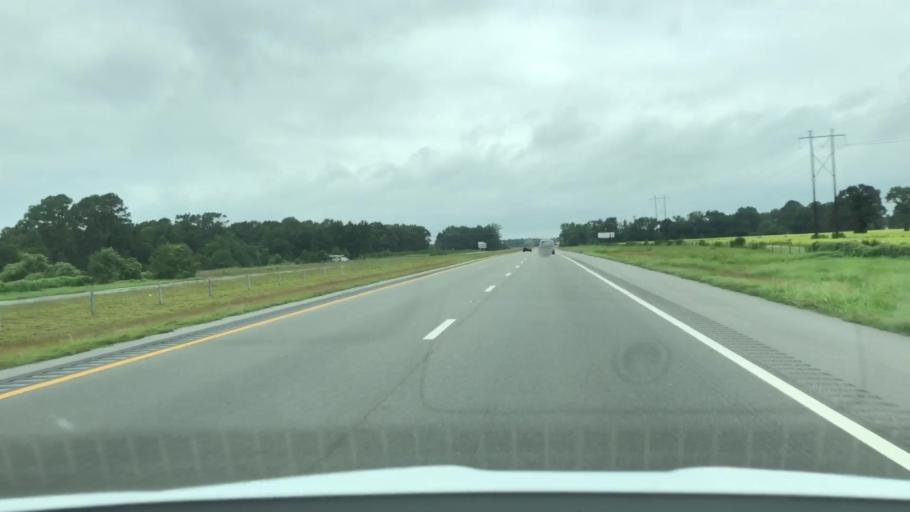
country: US
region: North Carolina
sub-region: Lenoir County
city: La Grange
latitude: 35.3159
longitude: -77.8297
